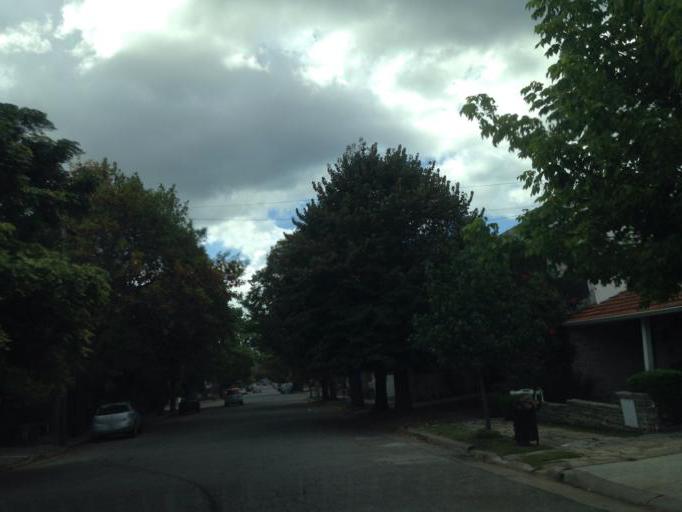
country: AR
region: Buenos Aires
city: Mar del Plata
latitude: -38.0178
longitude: -57.5503
